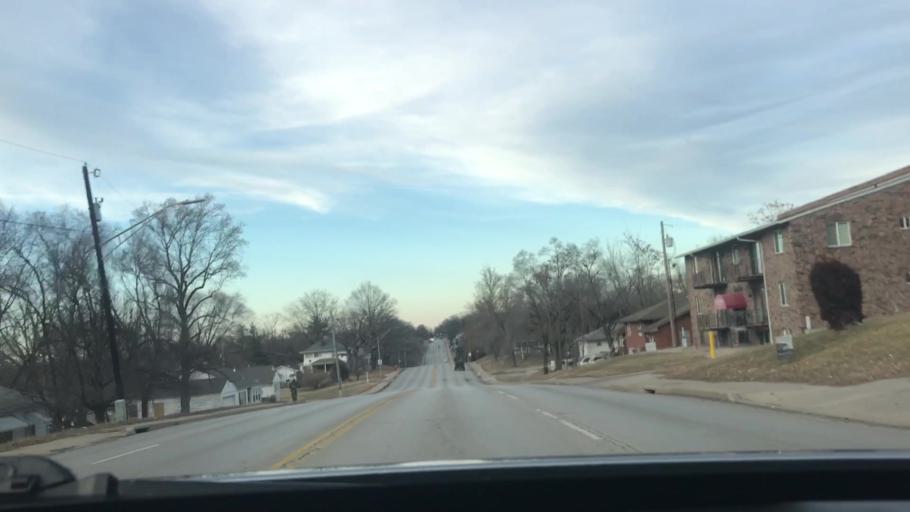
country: US
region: Missouri
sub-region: Jackson County
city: Independence
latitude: 39.0711
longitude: -94.4464
